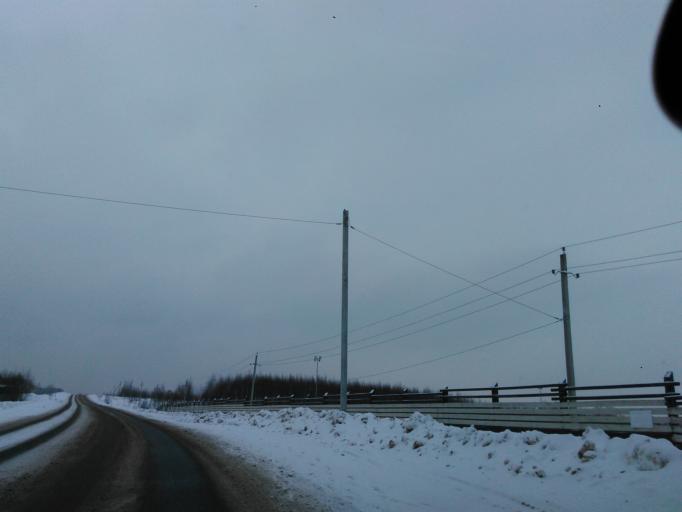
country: RU
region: Moskovskaya
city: Yakhroma
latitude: 56.2680
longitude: 37.4674
